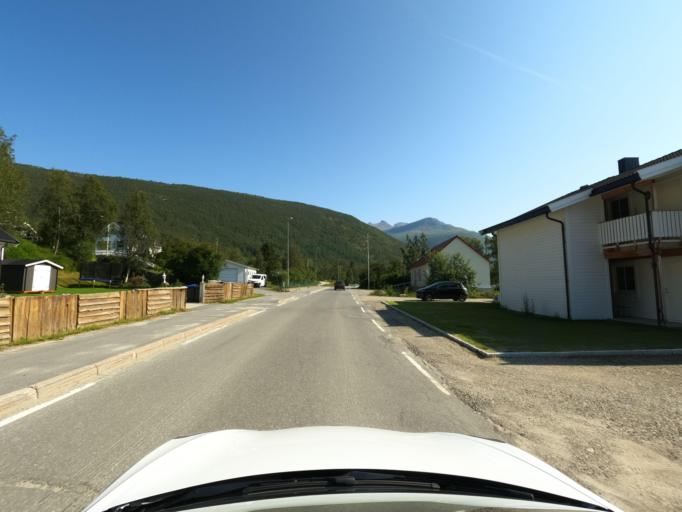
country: NO
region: Nordland
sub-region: Narvik
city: Bjerkvik
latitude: 68.3740
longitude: 17.6011
